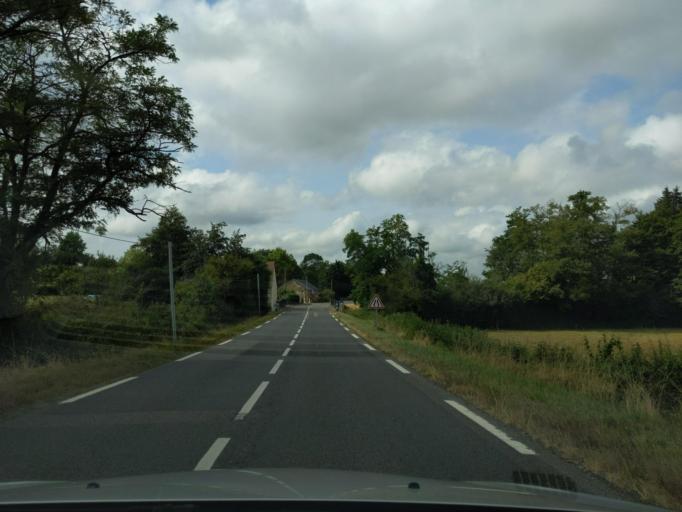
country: FR
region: Bourgogne
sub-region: Departement de la Nievre
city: Luzy
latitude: 46.7425
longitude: 3.9337
